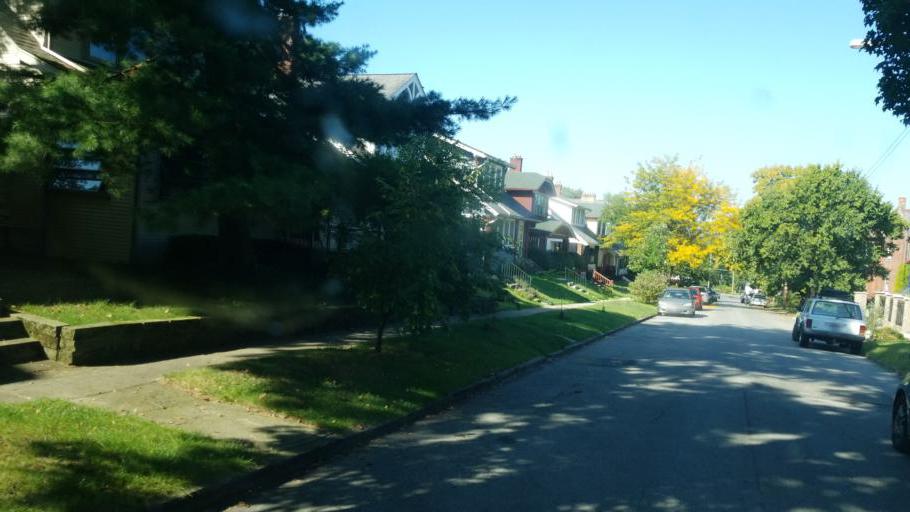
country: US
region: Ohio
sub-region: Franklin County
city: Grandview Heights
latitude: 40.0240
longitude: -83.0116
